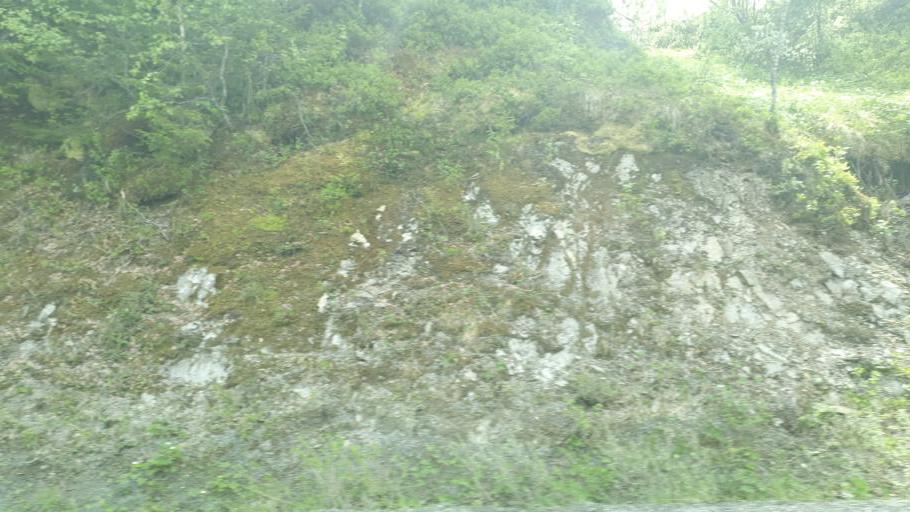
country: NO
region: Nord-Trondelag
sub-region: Leksvik
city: Leksvik
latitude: 63.6967
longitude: 10.4762
